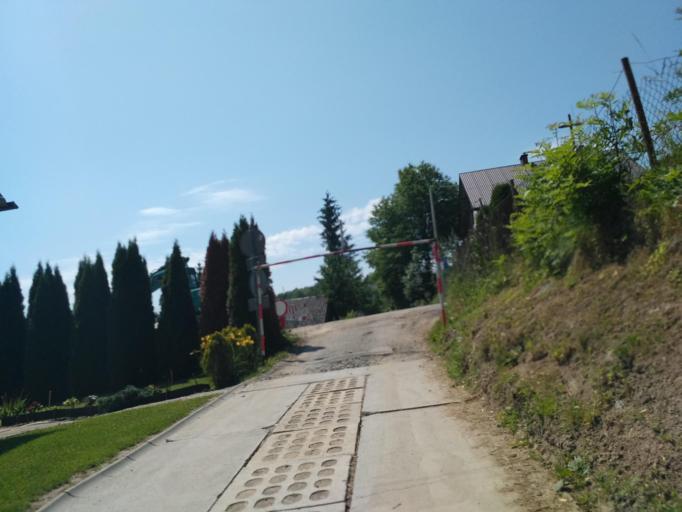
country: PL
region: Subcarpathian Voivodeship
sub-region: Powiat brzozowski
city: Golcowa
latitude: 49.8151
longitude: 22.0447
